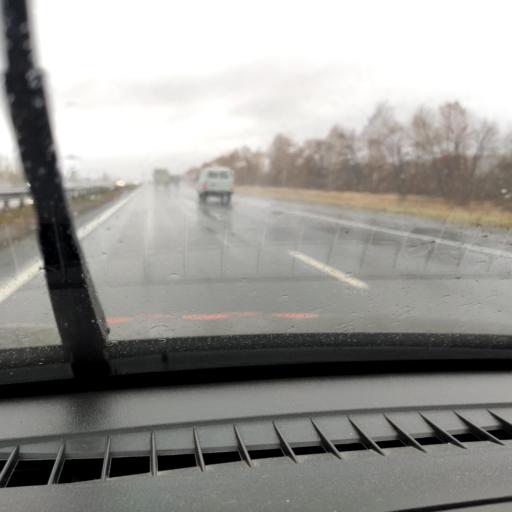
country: RU
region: Samara
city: Tol'yatti
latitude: 53.5764
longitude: 49.4311
